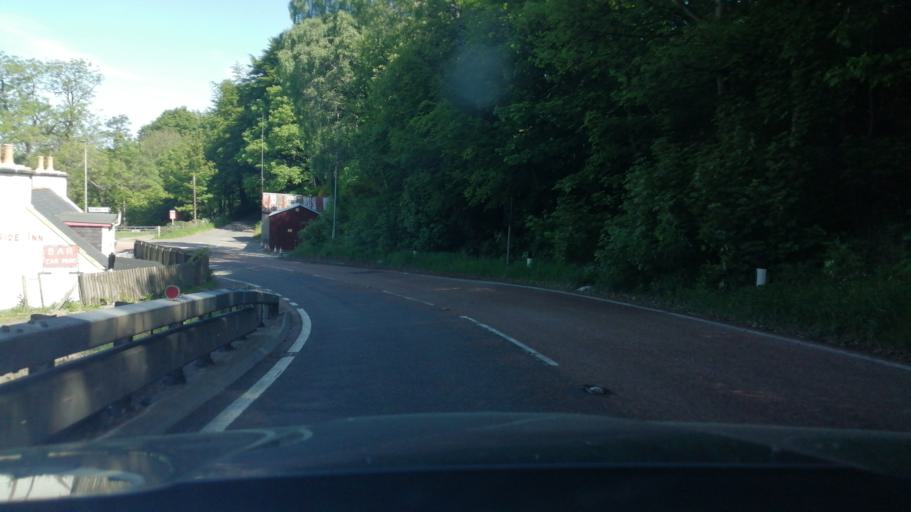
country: GB
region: Scotland
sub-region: Moray
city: Rothes
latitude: 57.4904
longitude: -3.1799
